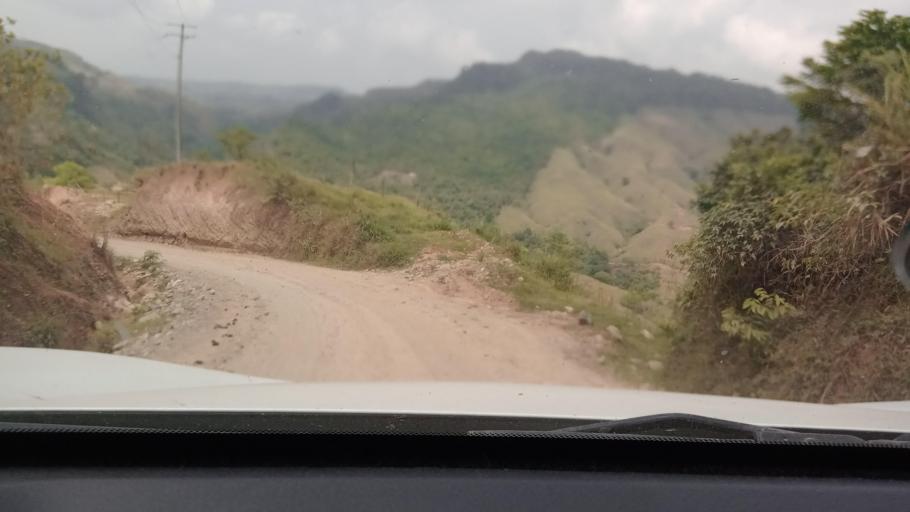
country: MX
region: Tabasco
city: Chontalpa
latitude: 17.4910
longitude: -93.6664
